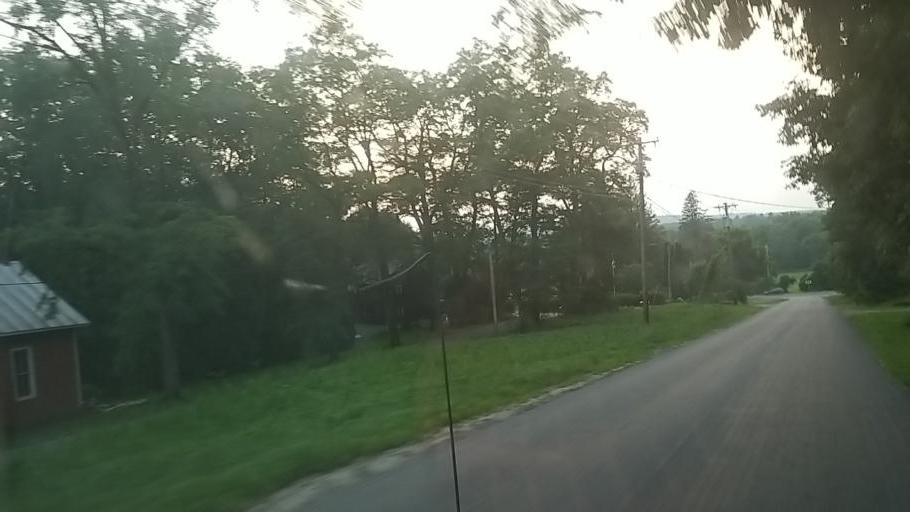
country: US
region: New York
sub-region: Montgomery County
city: Fonda
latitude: 42.9245
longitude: -74.4191
